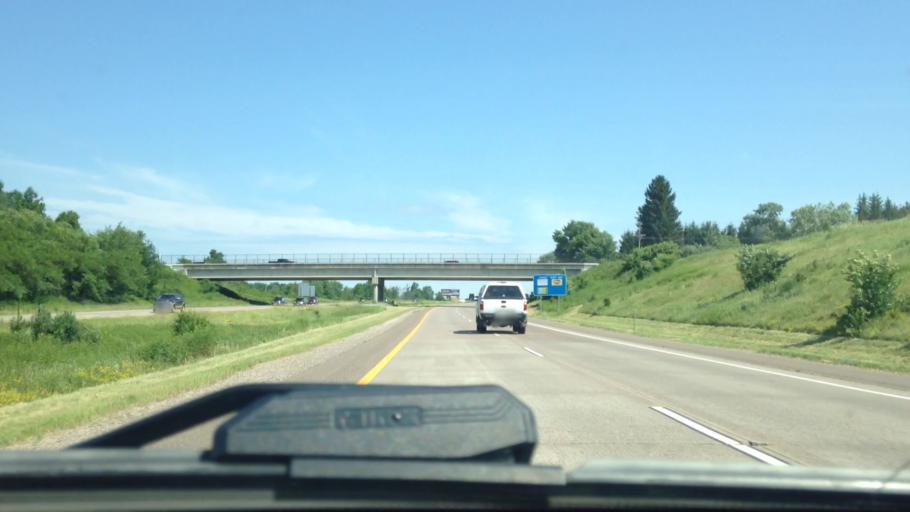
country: US
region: Wisconsin
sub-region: Barron County
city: Rice Lake
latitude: 45.4933
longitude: -91.7635
